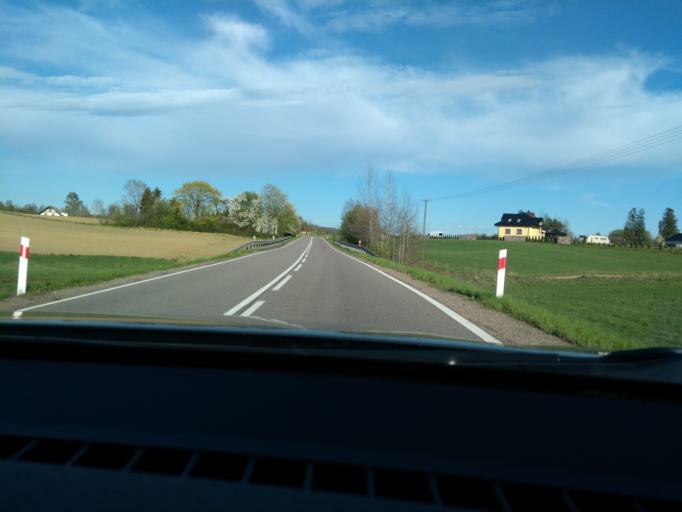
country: PL
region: Pomeranian Voivodeship
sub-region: Powiat leborski
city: Cewice
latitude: 54.3340
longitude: 17.7145
